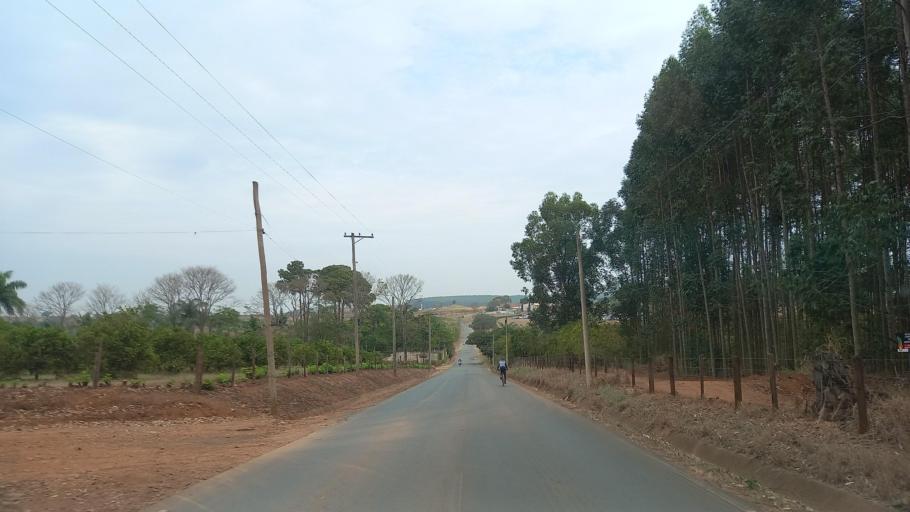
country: BR
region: Sao Paulo
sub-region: Moji-Guacu
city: Mogi-Gaucu
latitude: -22.3312
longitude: -46.8759
